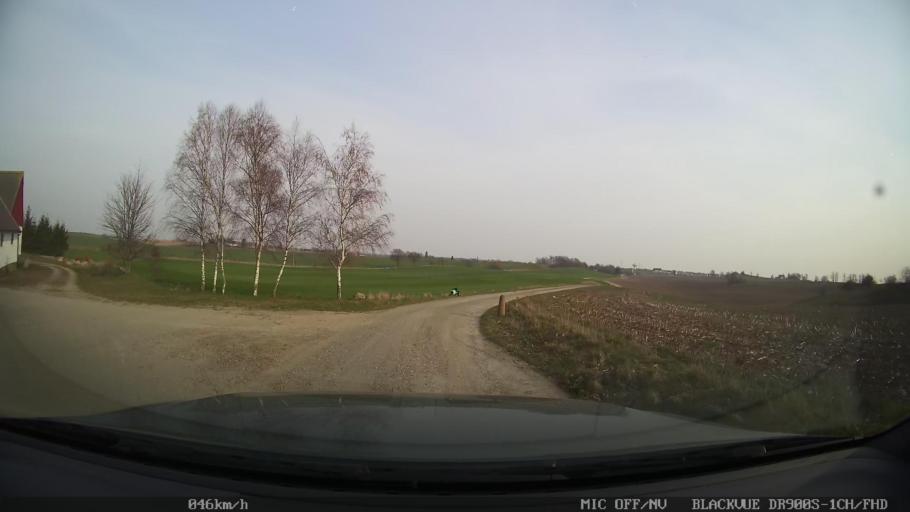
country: SE
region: Skane
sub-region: Ystads Kommun
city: Ystad
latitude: 55.4576
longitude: 13.7895
